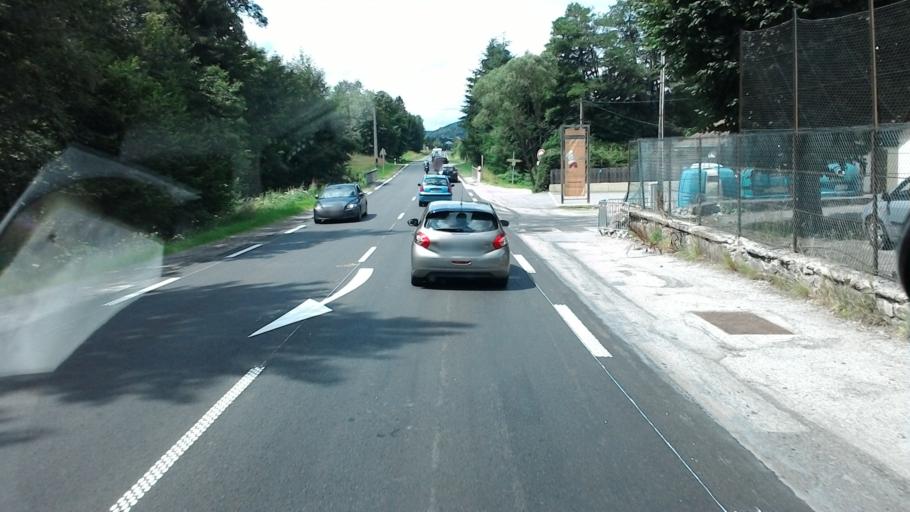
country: FR
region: Lorraine
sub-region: Departement des Vosges
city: Le Tholy
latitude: 48.0783
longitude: 6.7903
